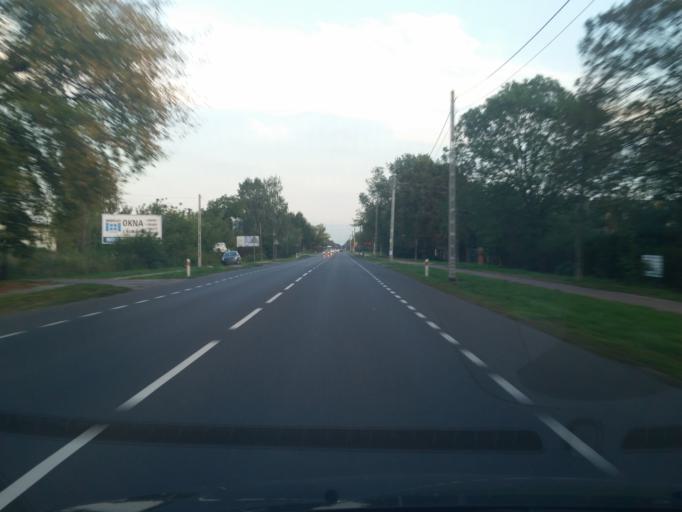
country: PL
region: Masovian Voivodeship
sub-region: Powiat legionowski
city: Jablonna
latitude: 52.3877
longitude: 20.8926
